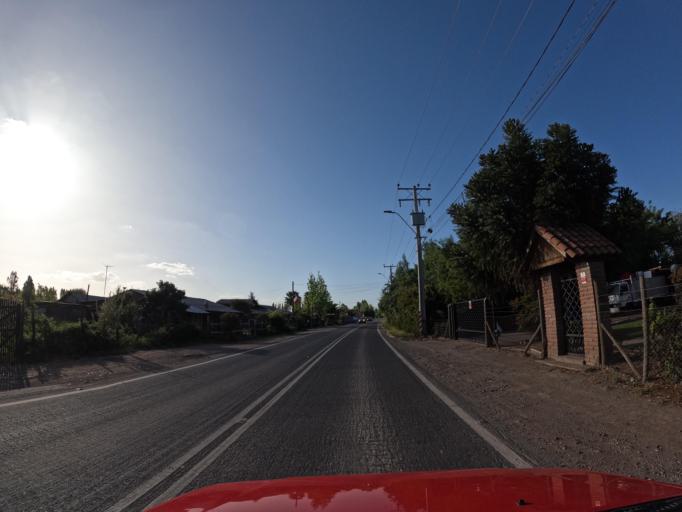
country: CL
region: O'Higgins
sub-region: Provincia de Colchagua
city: Santa Cruz
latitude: -34.6624
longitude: -71.3393
